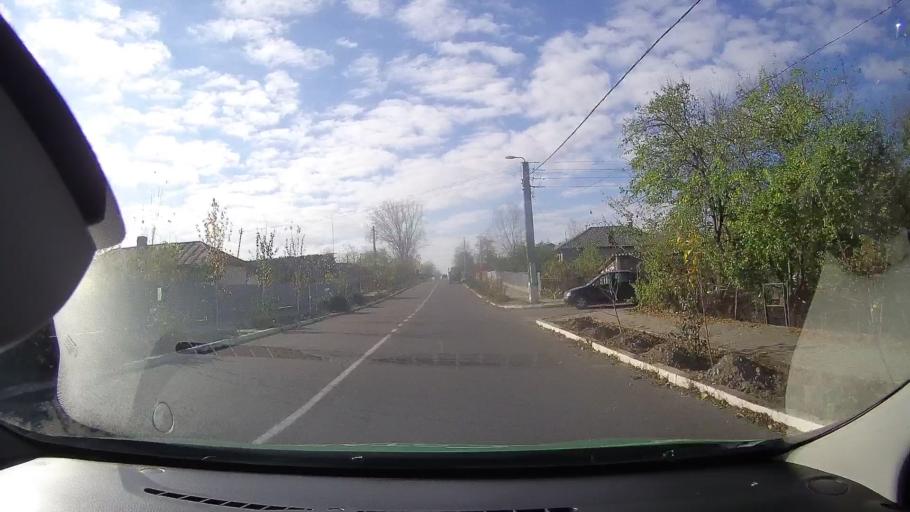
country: RO
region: Tulcea
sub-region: Comuna Mahmudia
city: Mahmudia
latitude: 45.0837
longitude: 29.0832
